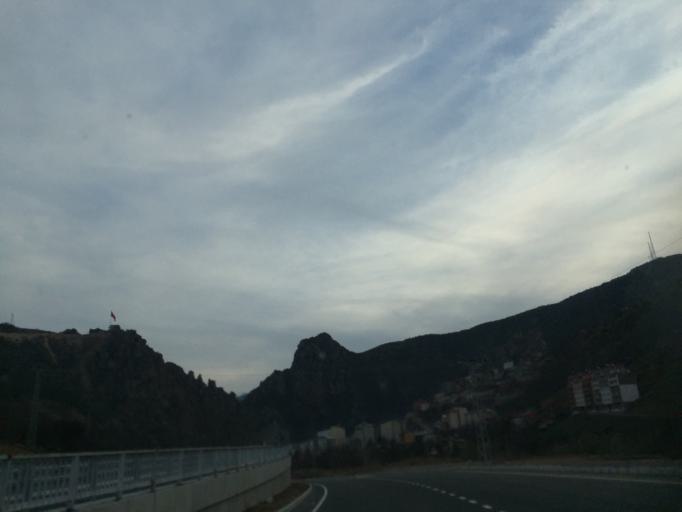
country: TR
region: Gumushane
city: Torul
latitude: 40.5658
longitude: 39.3004
